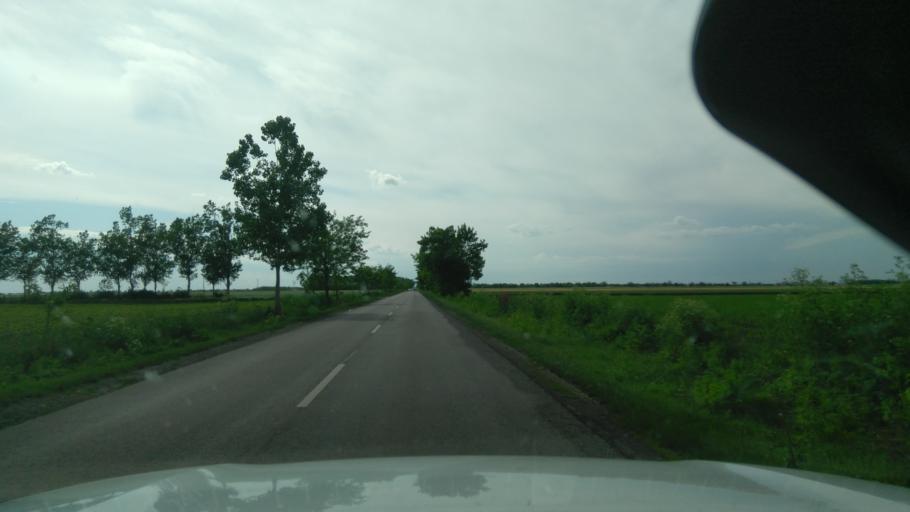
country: HU
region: Bekes
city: Medgyesegyhaza
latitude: 46.5110
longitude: 20.9879
